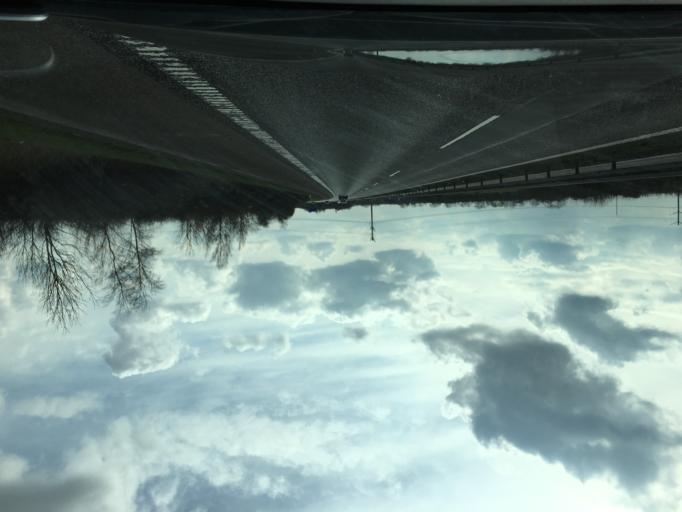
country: DK
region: South Denmark
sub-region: Vejen Kommune
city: Vejen
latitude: 55.4939
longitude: 9.1877
